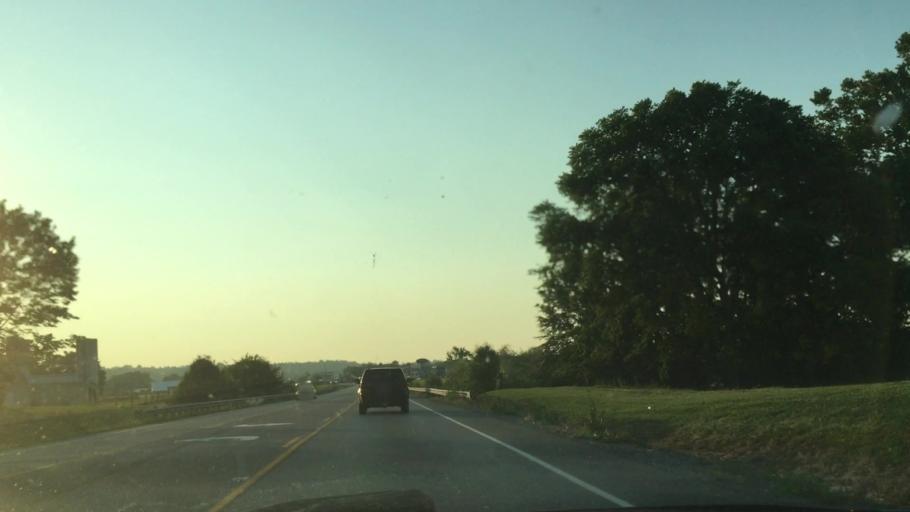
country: US
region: Kentucky
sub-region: Carroll County
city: Carrollton
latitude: 38.6523
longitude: -85.1273
